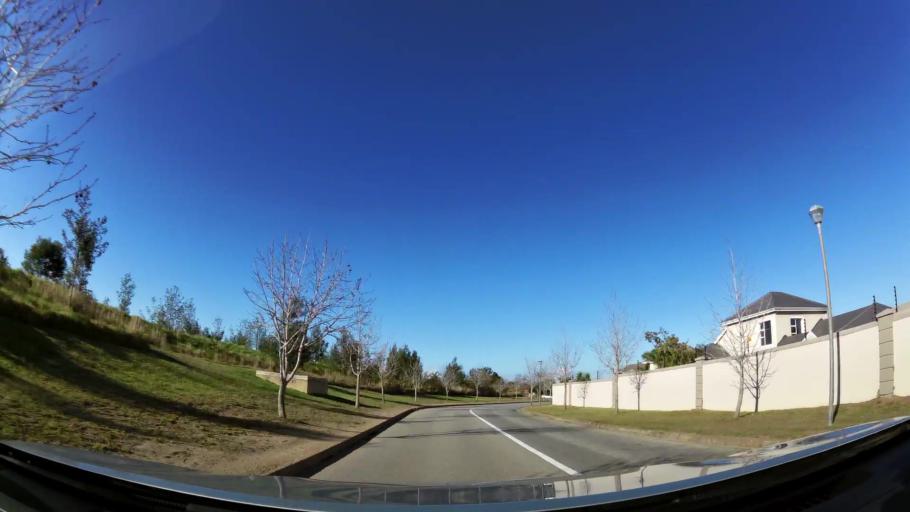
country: ZA
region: Western Cape
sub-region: Eden District Municipality
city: George
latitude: -33.9663
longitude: 22.4383
